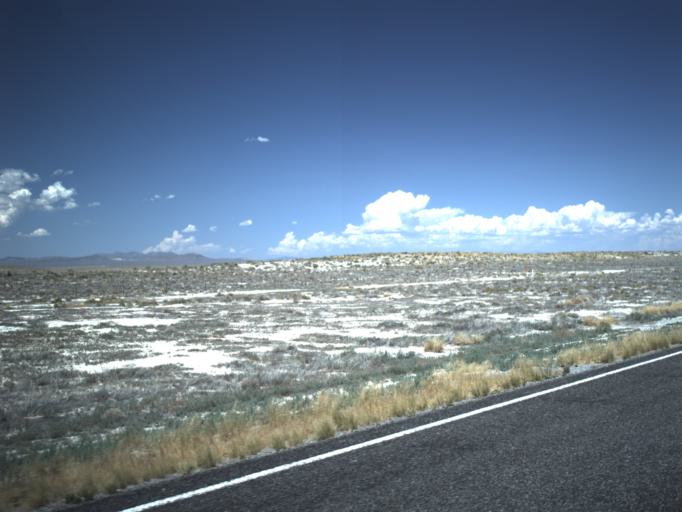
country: US
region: Utah
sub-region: Millard County
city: Delta
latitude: 39.1843
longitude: -113.0108
